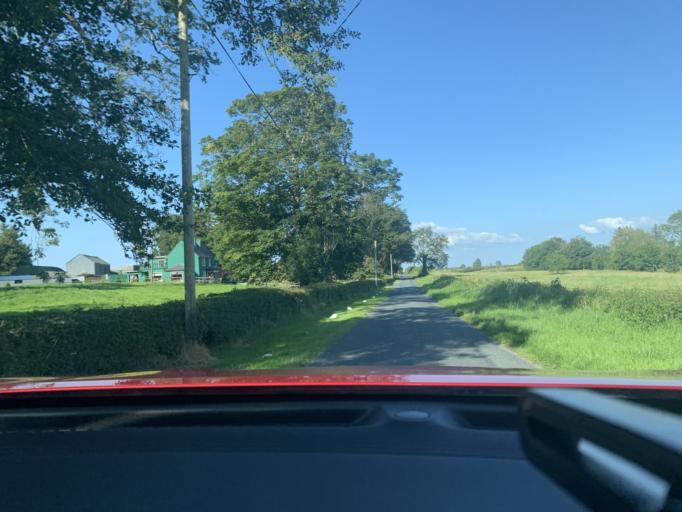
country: IE
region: Connaught
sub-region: Sligo
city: Tobercurry
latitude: 54.1380
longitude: -8.6957
